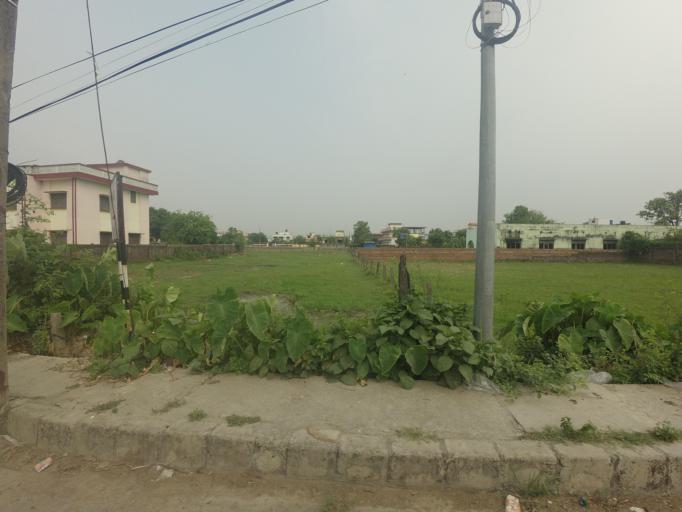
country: NP
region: Western Region
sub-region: Lumbini Zone
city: Bhairahawa
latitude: 27.4924
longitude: 83.4467
